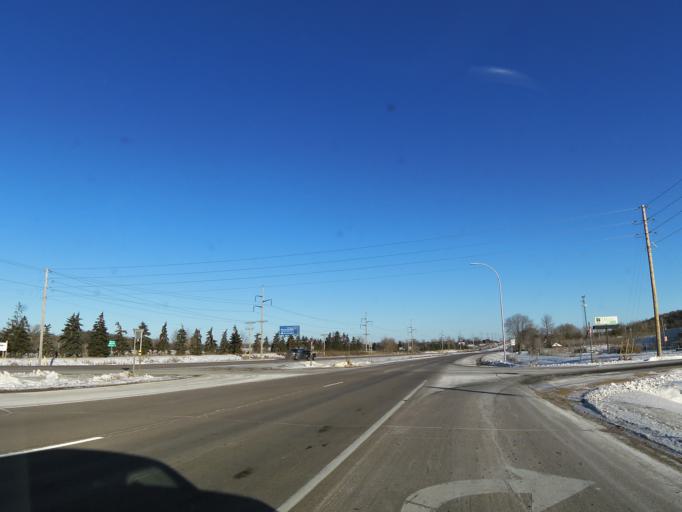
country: US
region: Minnesota
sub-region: Carver County
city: Carver
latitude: 44.7327
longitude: -93.5885
